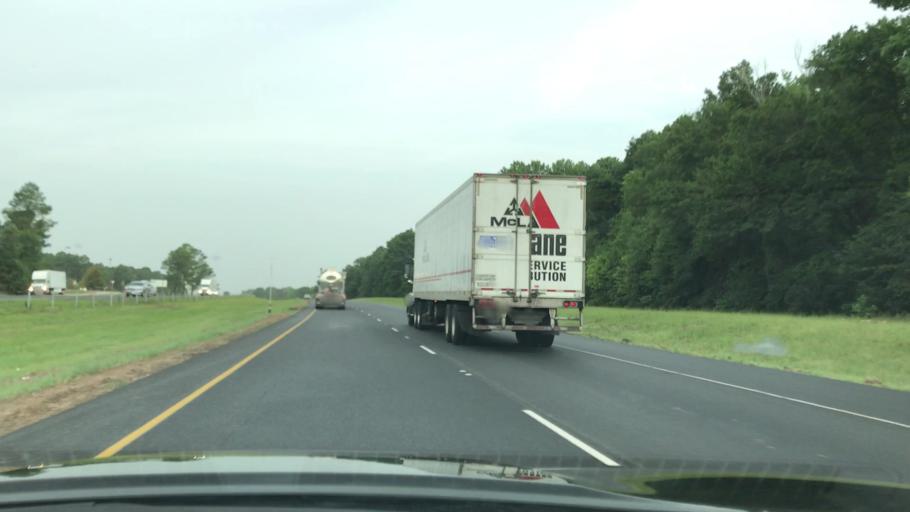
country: US
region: Louisiana
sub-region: Caddo Parish
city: Greenwood
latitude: 32.4513
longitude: -93.9967
